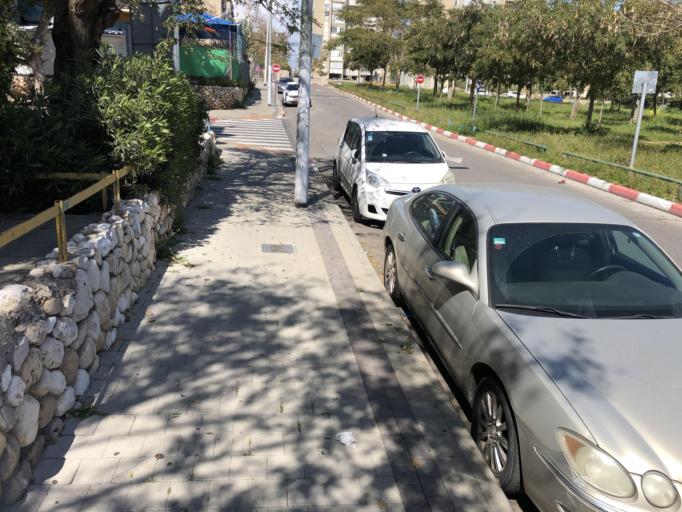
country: IL
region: Tel Aviv
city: Bat Yam
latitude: 32.0073
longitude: 34.7569
